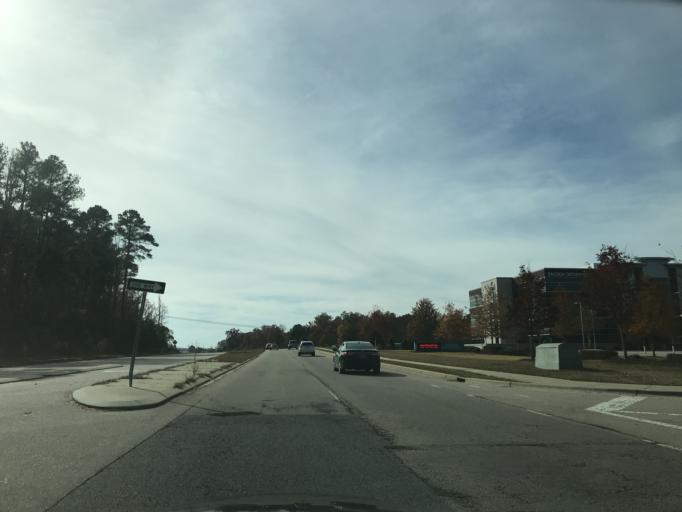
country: US
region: North Carolina
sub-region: Wake County
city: West Raleigh
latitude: 35.8224
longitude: -78.7088
